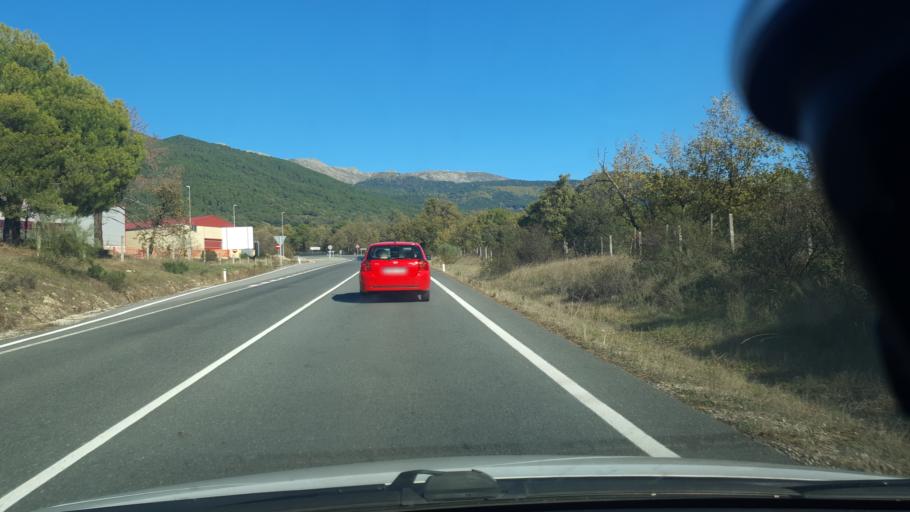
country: ES
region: Castille and Leon
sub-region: Provincia de Avila
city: Piedralaves
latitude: 40.2979
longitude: -4.7206
